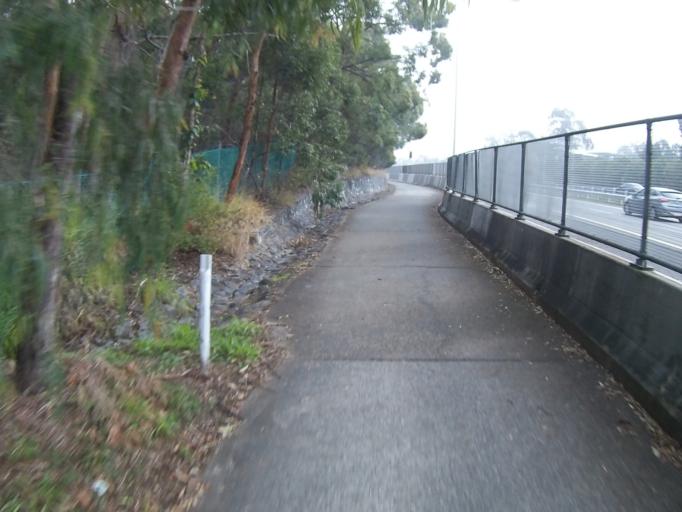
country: AU
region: Queensland
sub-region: Brisbane
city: Nathan
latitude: -27.5482
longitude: 153.0646
